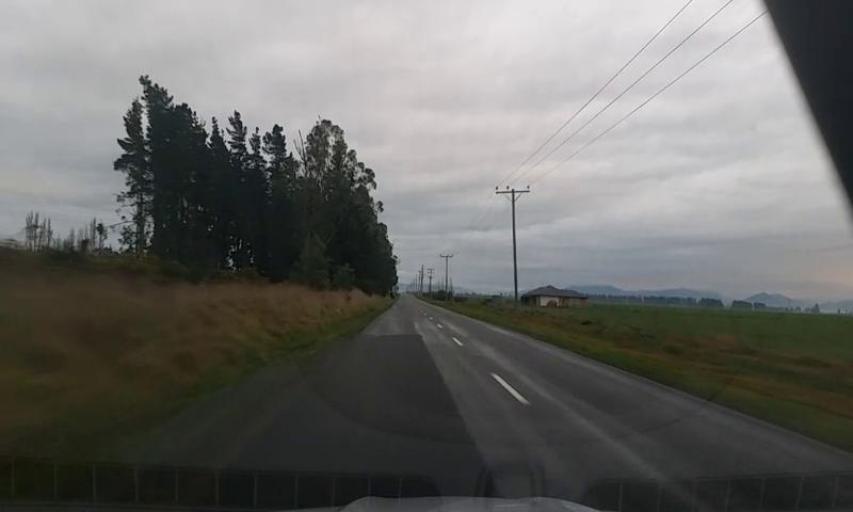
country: NZ
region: Canterbury
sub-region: Ashburton District
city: Ashburton
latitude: -43.7502
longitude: 171.8269
